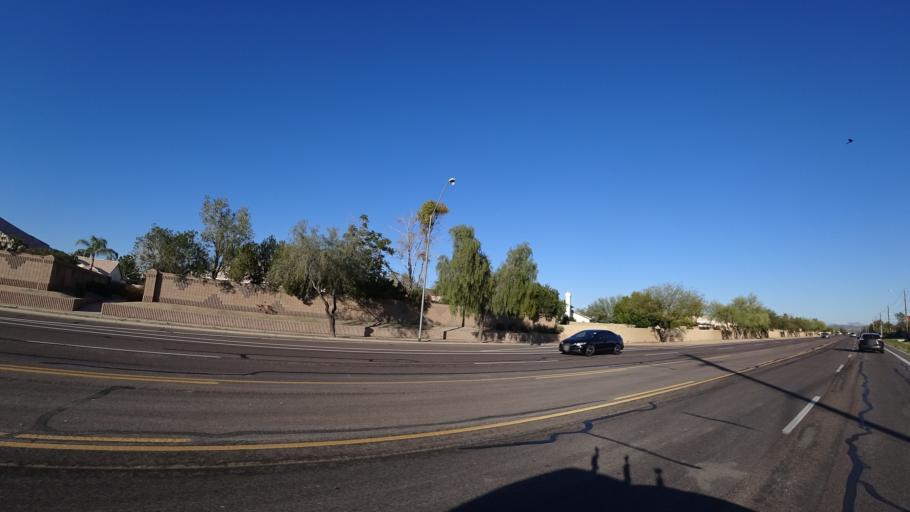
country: US
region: Arizona
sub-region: Maricopa County
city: Peoria
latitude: 33.7124
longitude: -112.1681
